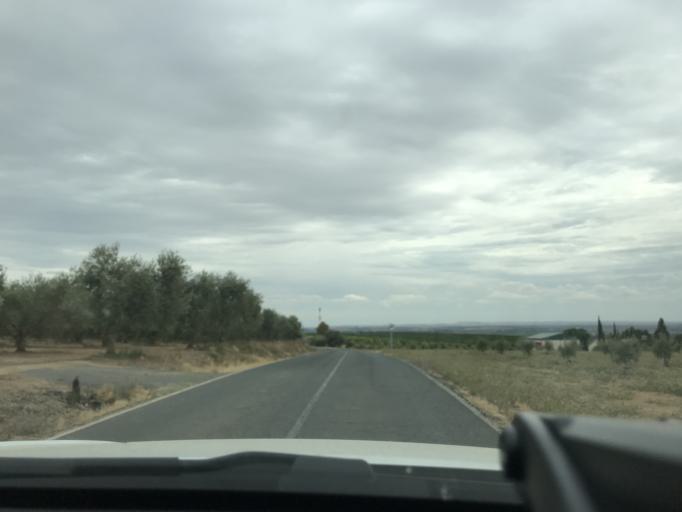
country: ES
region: Andalusia
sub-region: Provincia de Sevilla
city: Villanueva del Rio y Minas
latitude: 37.6439
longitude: -5.7075
